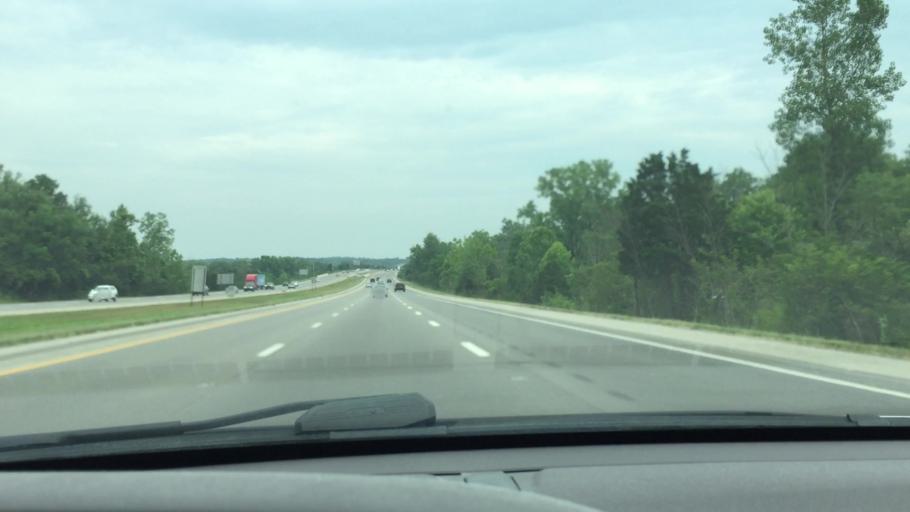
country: US
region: Ohio
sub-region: Warren County
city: Kings Mills
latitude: 39.3669
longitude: -84.2537
